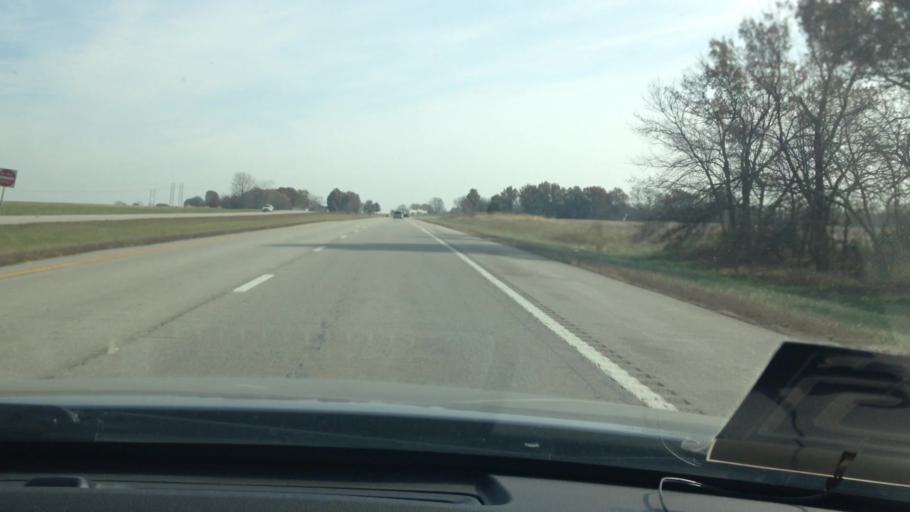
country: US
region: Missouri
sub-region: Cass County
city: Garden City
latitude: 38.6015
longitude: -94.2659
